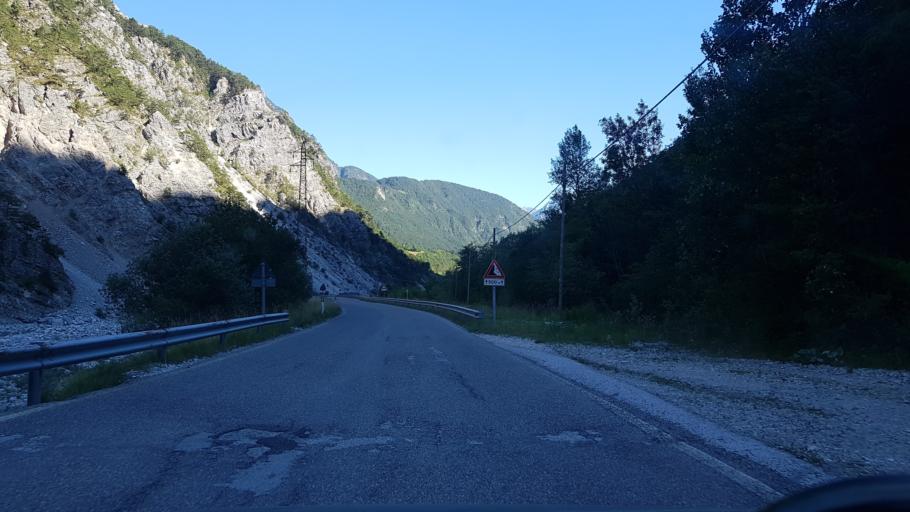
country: IT
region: Friuli Venezia Giulia
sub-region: Provincia di Udine
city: Moggio Udinese
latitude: 46.4394
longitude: 13.1958
